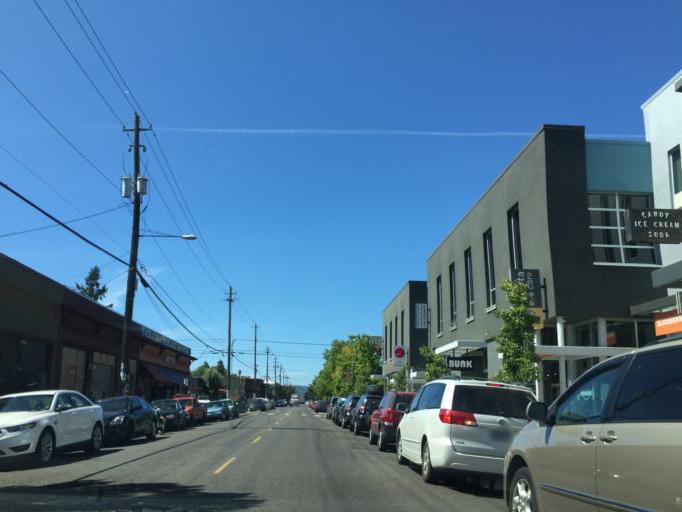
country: US
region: Oregon
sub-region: Multnomah County
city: Portland
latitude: 45.5591
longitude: -122.6439
